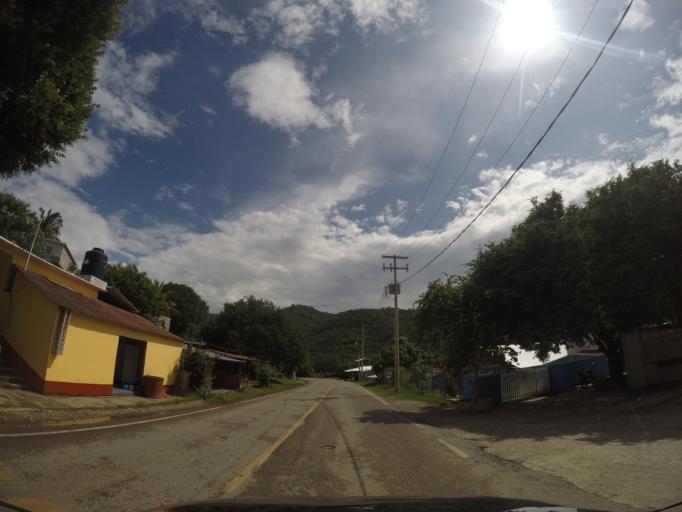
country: MX
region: Oaxaca
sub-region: San Jeronimo Coatlan
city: San Cristobal Honduras
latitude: 16.3550
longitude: -97.0954
